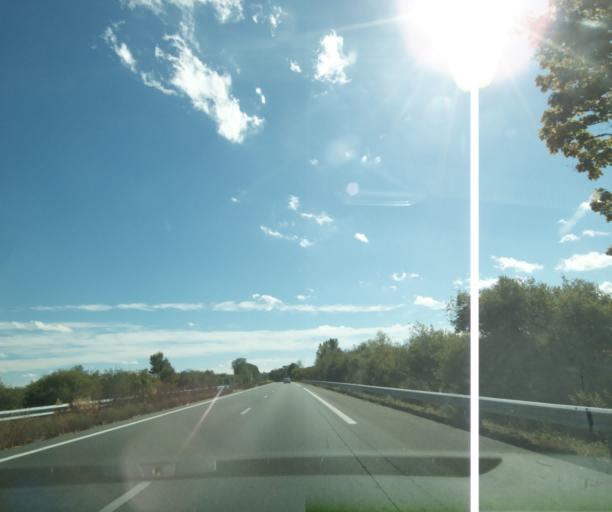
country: FR
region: Aquitaine
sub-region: Departement du Lot-et-Garonne
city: Damazan
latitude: 44.2927
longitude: 0.2624
